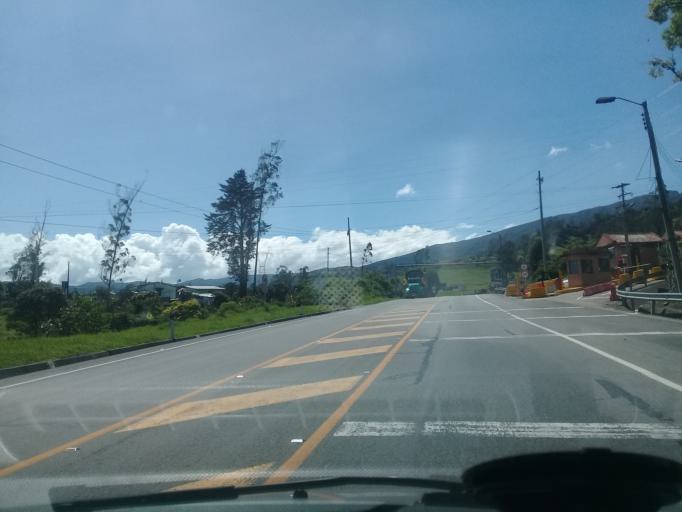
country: CO
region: Cundinamarca
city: Chipaque
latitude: 4.4542
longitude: -74.0496
